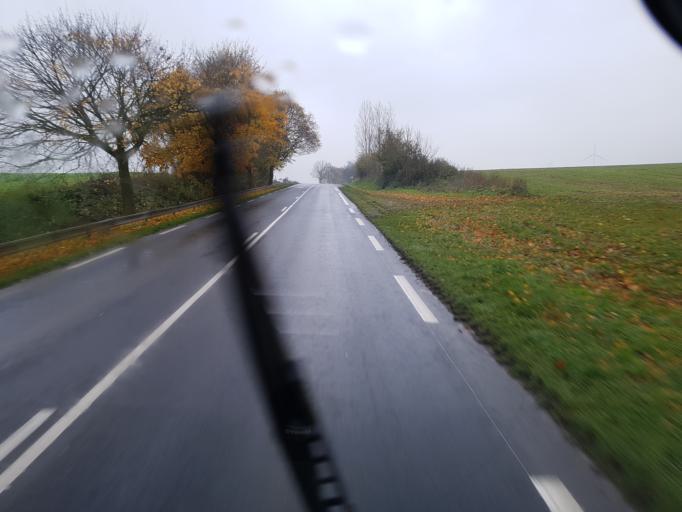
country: FR
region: Picardie
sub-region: Departement de l'Aisne
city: Saint-Quentin
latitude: 49.8741
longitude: 3.2697
